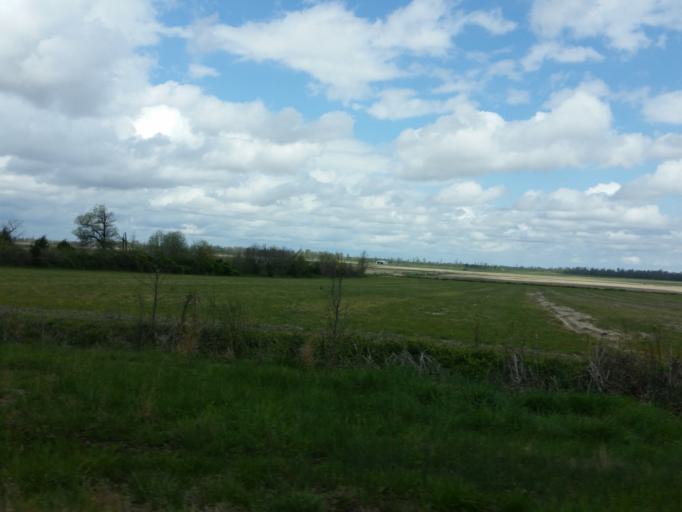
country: US
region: Arkansas
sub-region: Greene County
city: Paragould
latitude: 36.2188
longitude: -90.5577
